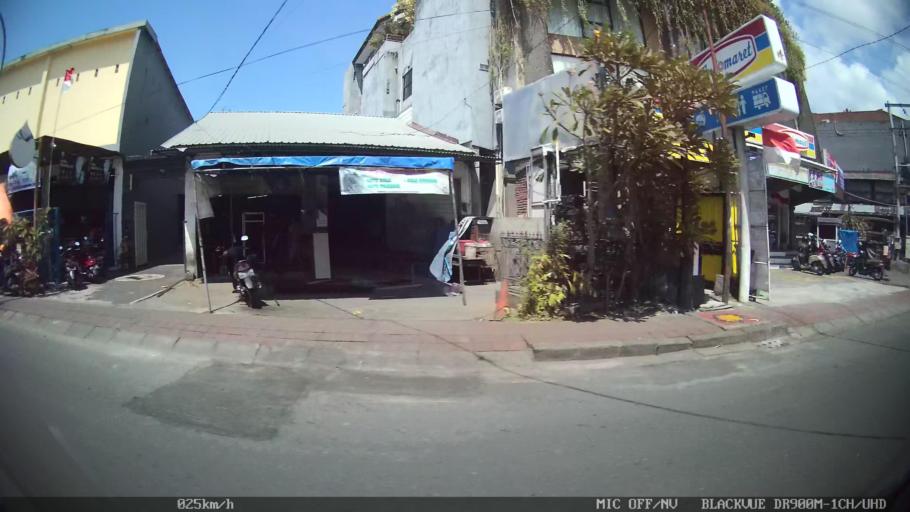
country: ID
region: Bali
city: Kuta
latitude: -8.6975
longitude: 115.1735
